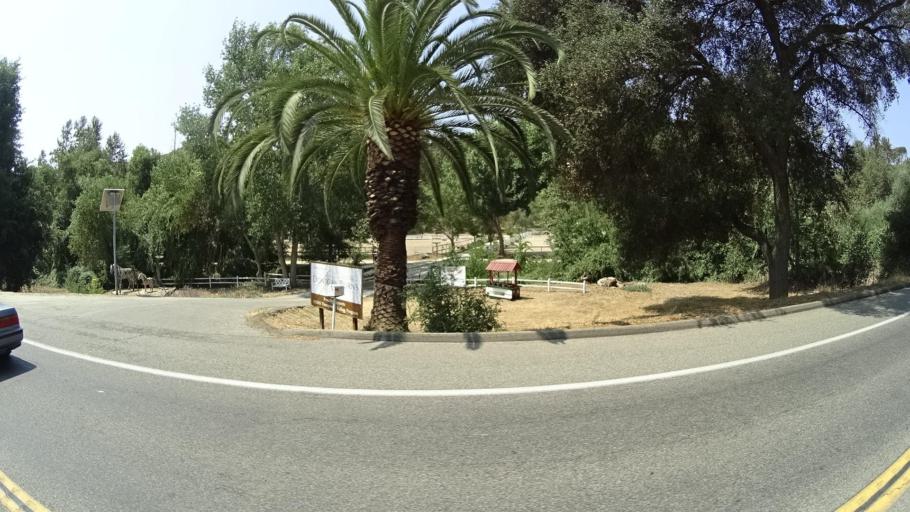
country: US
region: California
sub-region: San Diego County
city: Bonsall
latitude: 33.3109
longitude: -117.2292
